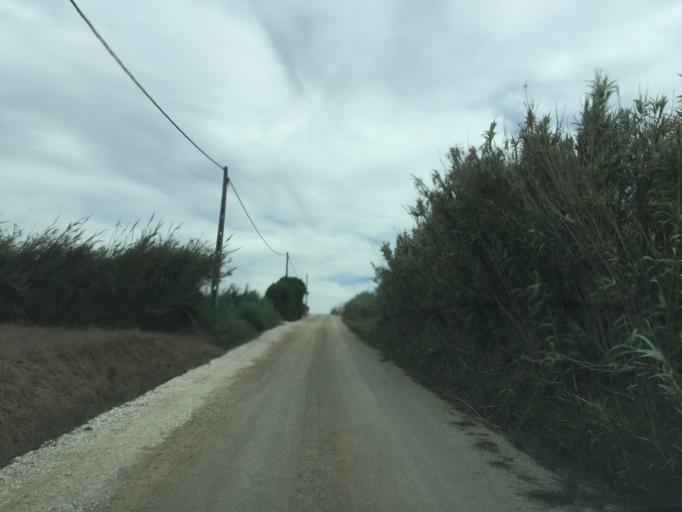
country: PT
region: Lisbon
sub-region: Lourinha
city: Lourinha
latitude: 39.1972
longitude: -9.3441
